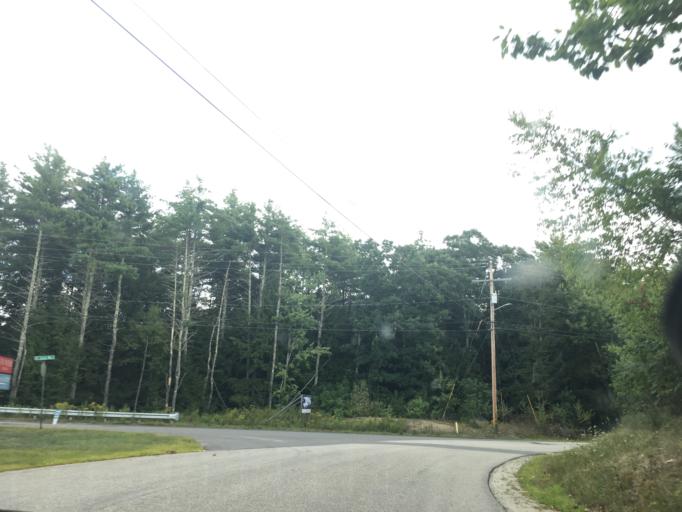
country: US
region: New Hampshire
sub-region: Rockingham County
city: Exeter
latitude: 42.9950
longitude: -70.9796
